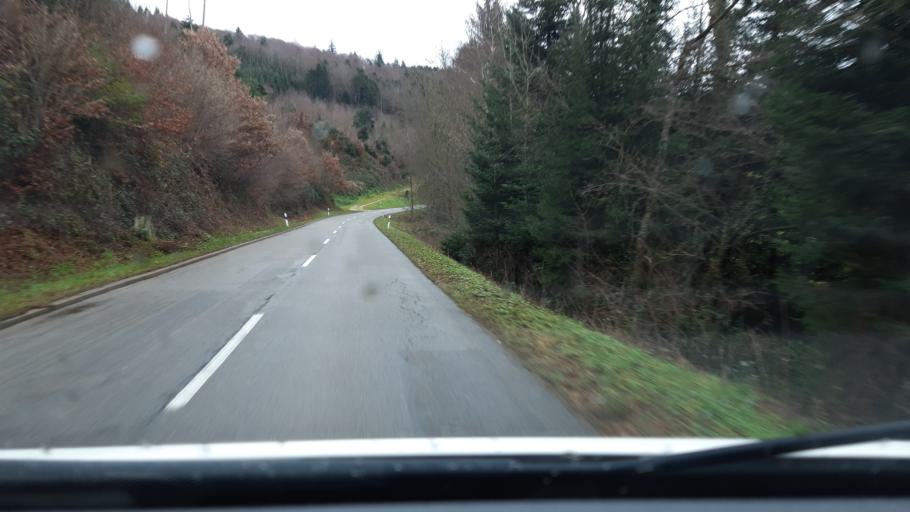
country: DE
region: Baden-Wuerttemberg
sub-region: Freiburg Region
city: Solden
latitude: 47.9201
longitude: 7.8066
